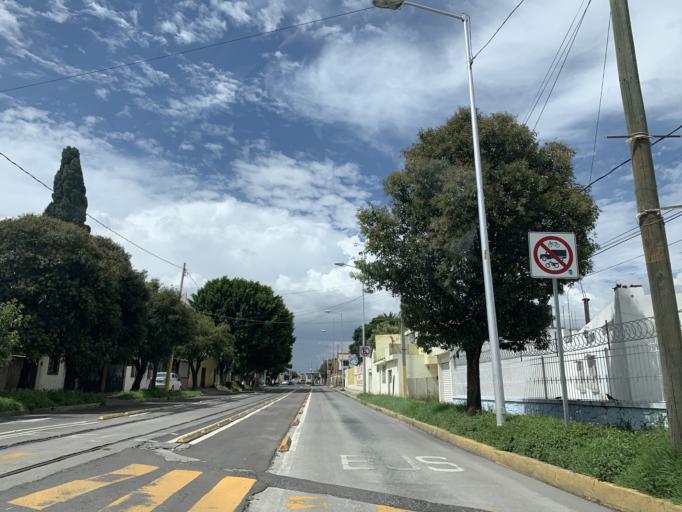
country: MX
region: Puebla
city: Puebla
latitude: 19.0619
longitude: -98.1955
